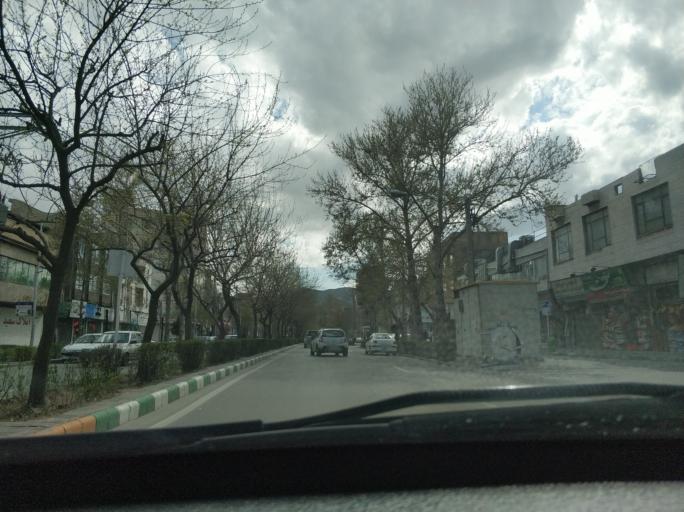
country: IR
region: Razavi Khorasan
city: Mashhad
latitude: 36.2735
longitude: 59.5910
